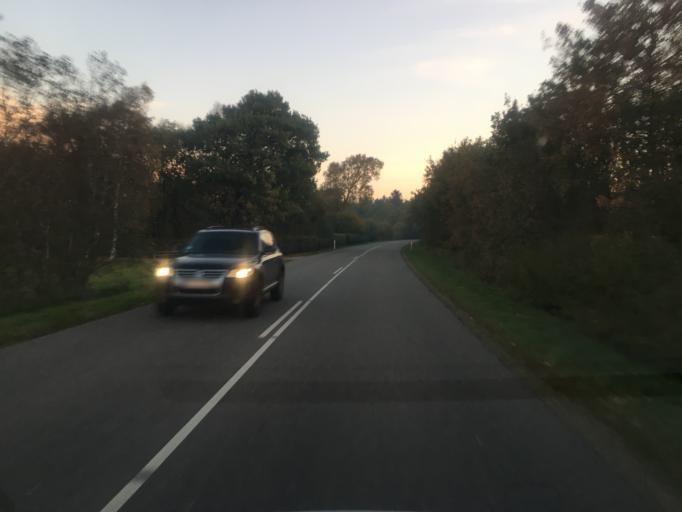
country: DE
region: Schleswig-Holstein
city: Bramstedtlund
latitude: 54.9616
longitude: 9.1122
